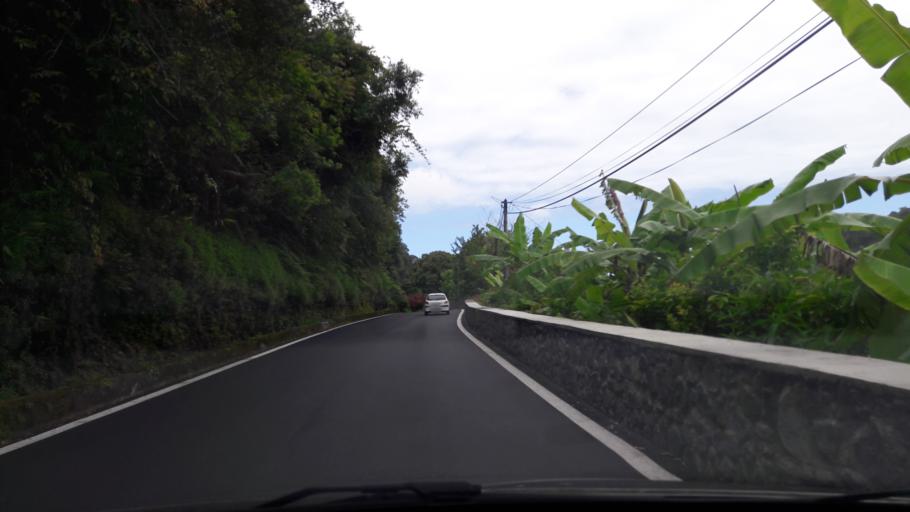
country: RE
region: Reunion
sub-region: Reunion
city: Saint-Andre
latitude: -20.9882
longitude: 55.6181
